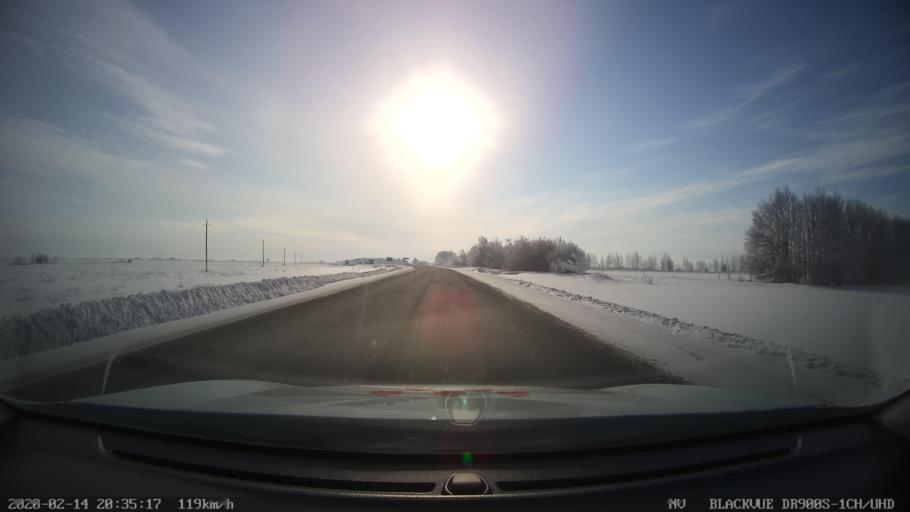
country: RU
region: Tatarstan
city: Kuybyshevskiy Zaton
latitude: 55.3844
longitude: 48.9815
